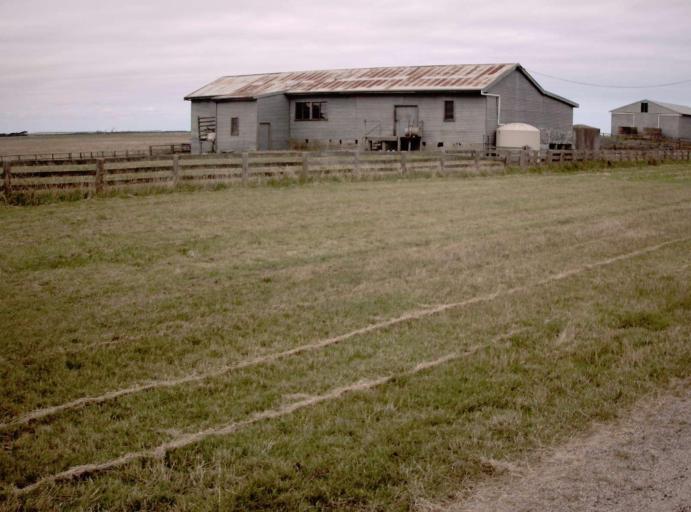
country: AU
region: Victoria
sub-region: Wellington
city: Sale
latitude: -38.5433
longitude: 146.9420
